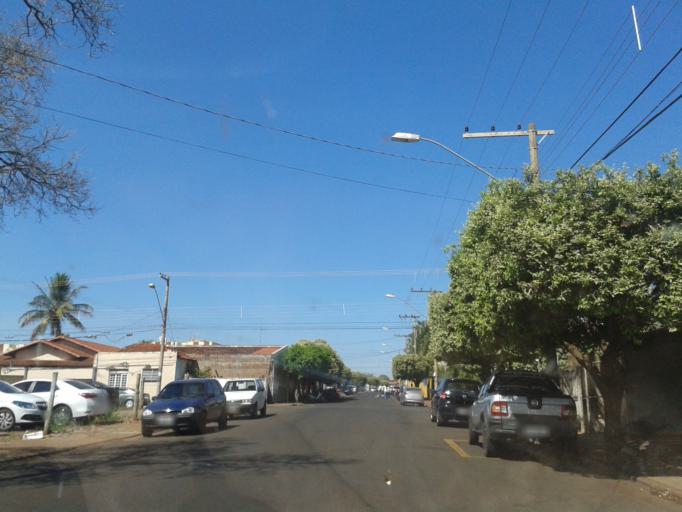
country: BR
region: Minas Gerais
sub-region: Ituiutaba
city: Ituiutaba
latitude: -18.9803
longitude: -49.4563
